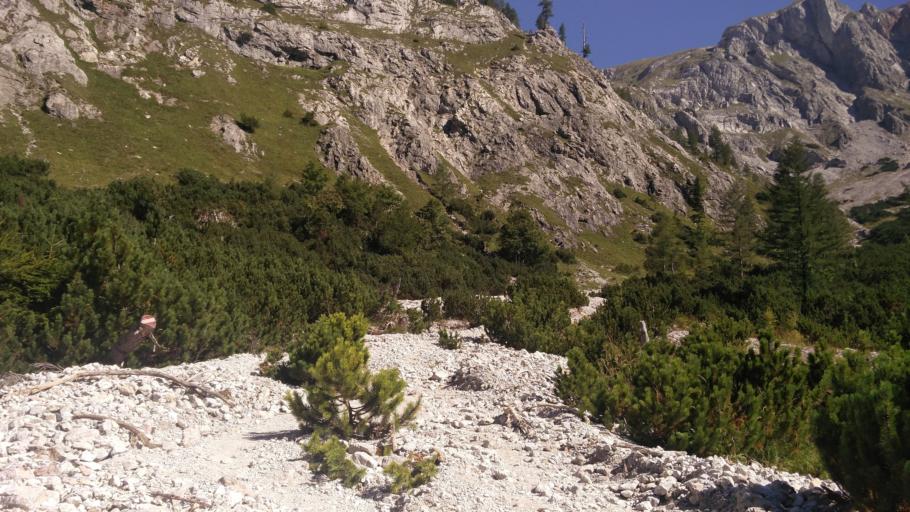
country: AT
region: Styria
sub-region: Politischer Bezirk Bruck-Muerzzuschlag
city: Sankt Ilgen
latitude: 47.6027
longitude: 15.1379
